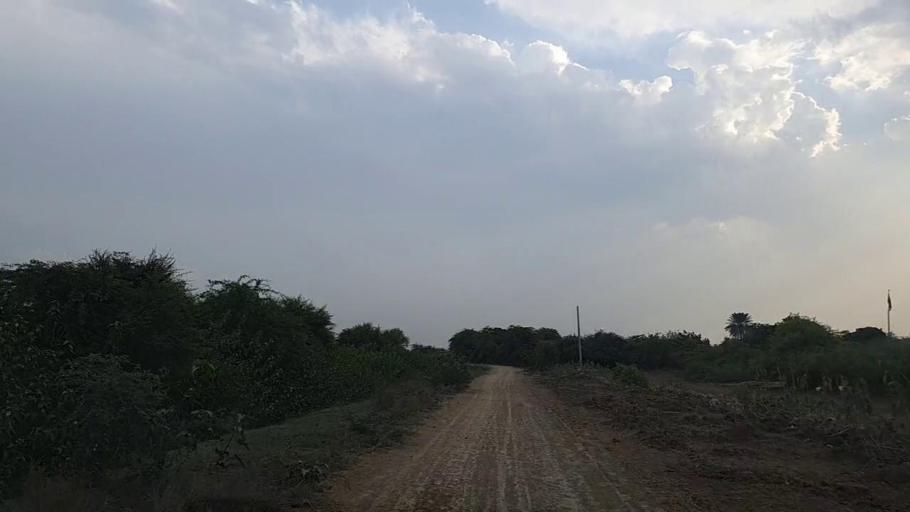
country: PK
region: Sindh
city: Daro Mehar
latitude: 24.7658
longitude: 68.1538
